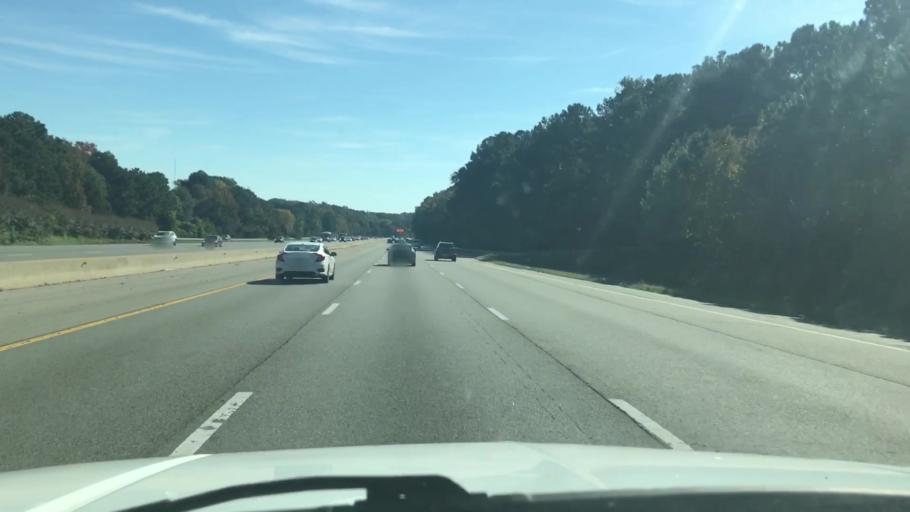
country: US
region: Virginia
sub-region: Henrico County
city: Tuckahoe
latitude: 37.6235
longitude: -77.5528
